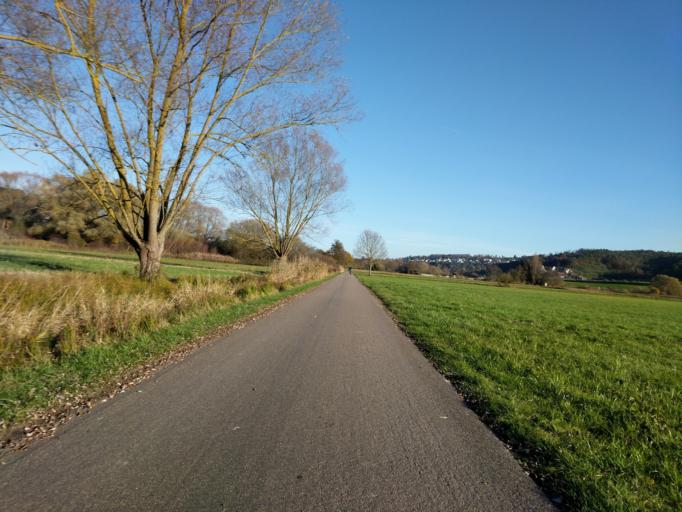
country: DE
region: Baden-Wuerttemberg
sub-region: Tuebingen Region
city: Tuebingen
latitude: 48.5229
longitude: 9.0086
